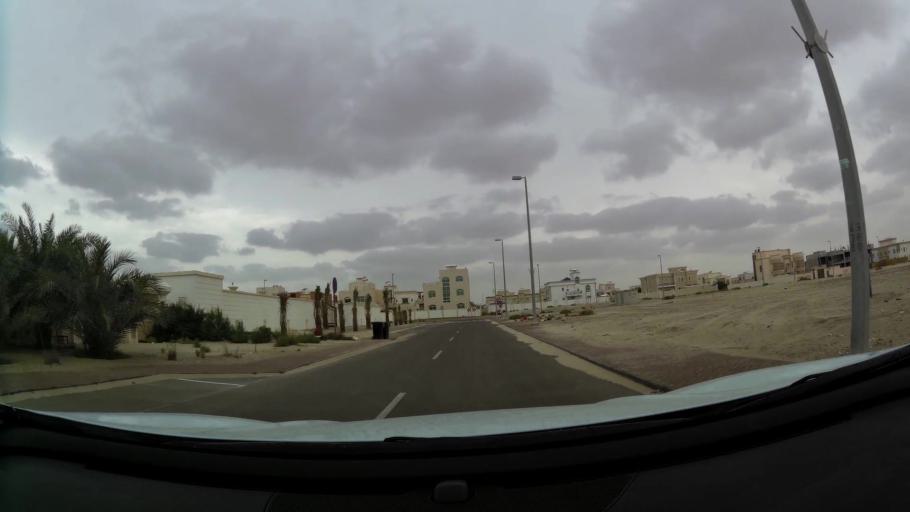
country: AE
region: Abu Dhabi
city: Abu Dhabi
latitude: 24.3724
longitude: 54.6435
